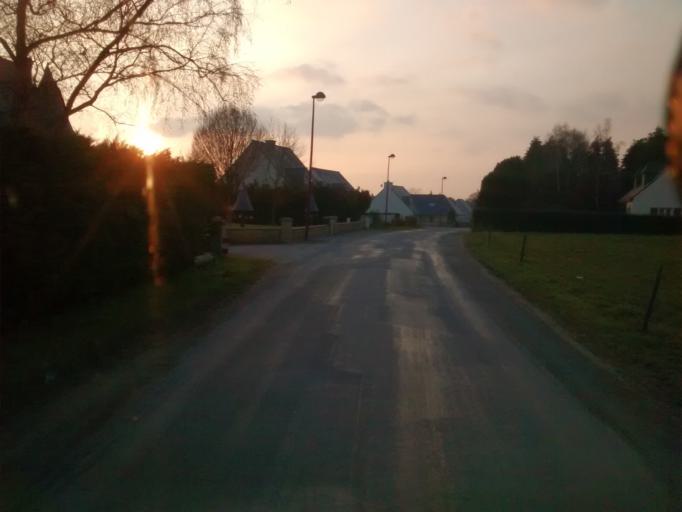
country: FR
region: Brittany
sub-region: Departement du Morbihan
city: Meneac
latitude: 48.1417
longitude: -2.4612
